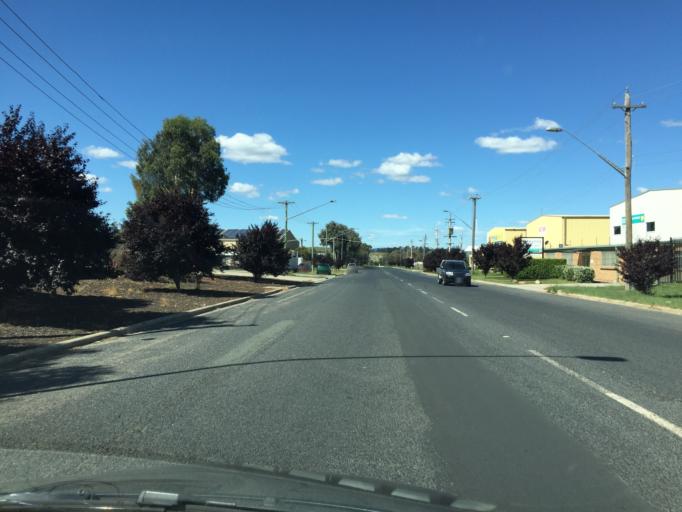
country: AU
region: Australian Capital Territory
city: Macarthur
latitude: -35.3876
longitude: 149.1717
